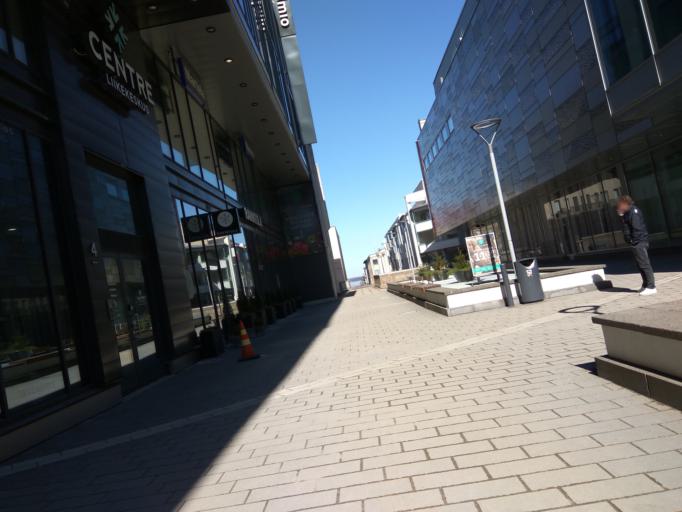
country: FI
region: South Karelia
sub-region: Lappeenranta
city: Lappeenranta
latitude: 61.0571
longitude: 28.1926
